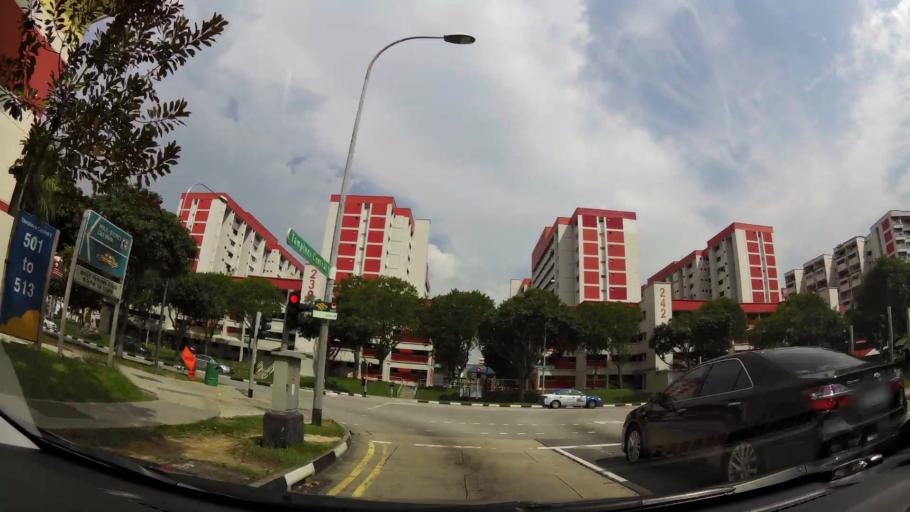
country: SG
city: Singapore
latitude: 1.3544
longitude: 103.9460
